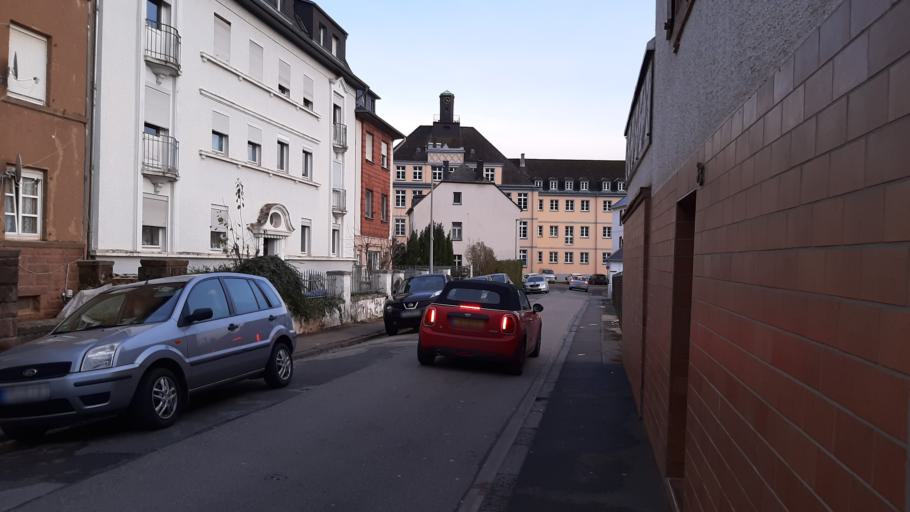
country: DE
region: Rheinland-Pfalz
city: Trier
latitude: 49.7533
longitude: 6.6194
